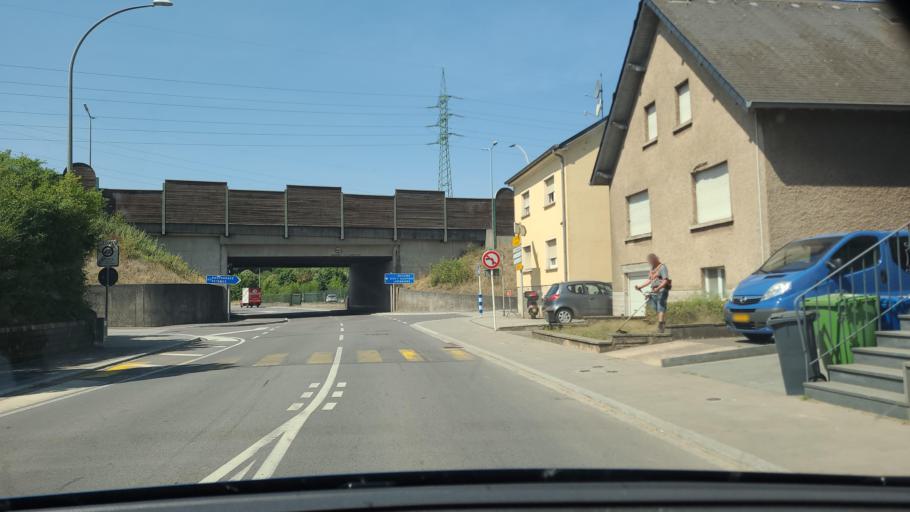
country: LU
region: Luxembourg
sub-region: Canton d'Esch-sur-Alzette
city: Sanem
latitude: 49.5442
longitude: 5.9194
